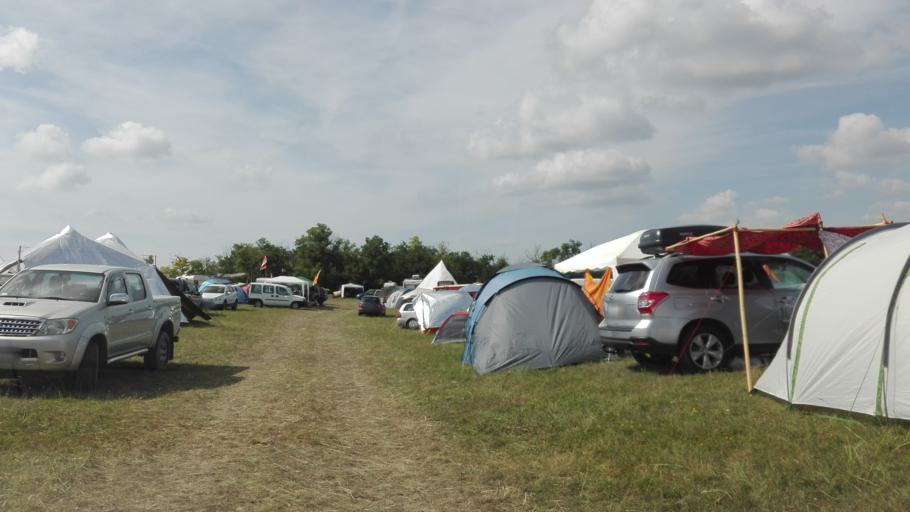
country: HU
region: Tolna
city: Ozora
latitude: 46.7682
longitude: 18.4309
